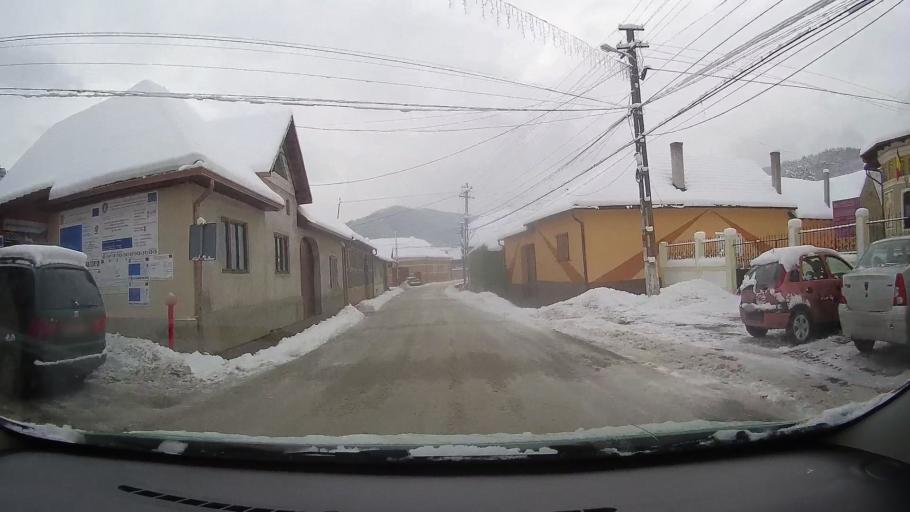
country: RO
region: Alba
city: Pianu de Sus
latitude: 45.8953
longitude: 23.4827
